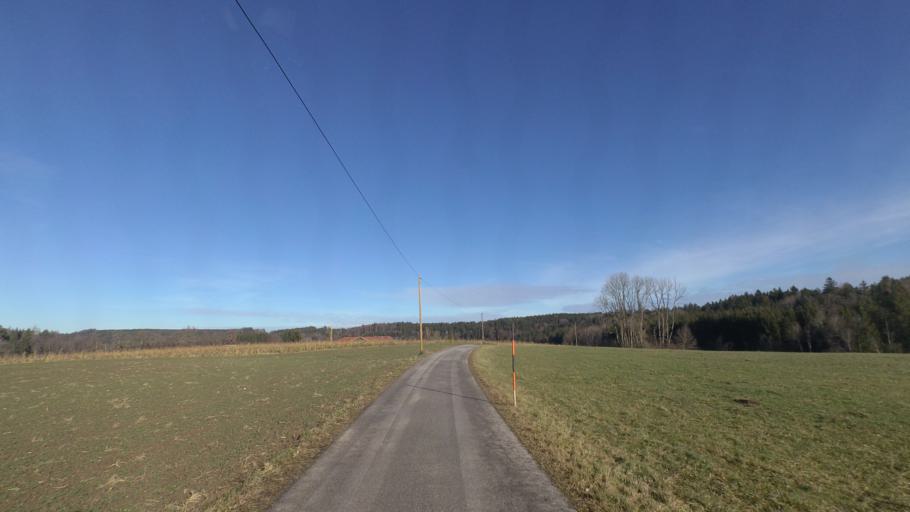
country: DE
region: Bavaria
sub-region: Upper Bavaria
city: Grabenstatt
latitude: 47.8578
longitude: 12.5508
